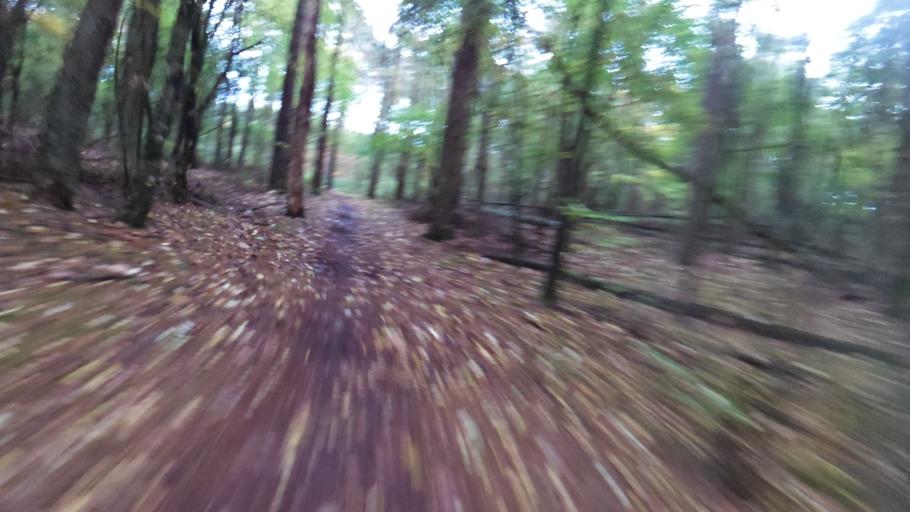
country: NL
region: Gelderland
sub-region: Gemeente Renkum
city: Oosterbeek
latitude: 52.0030
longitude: 5.8244
